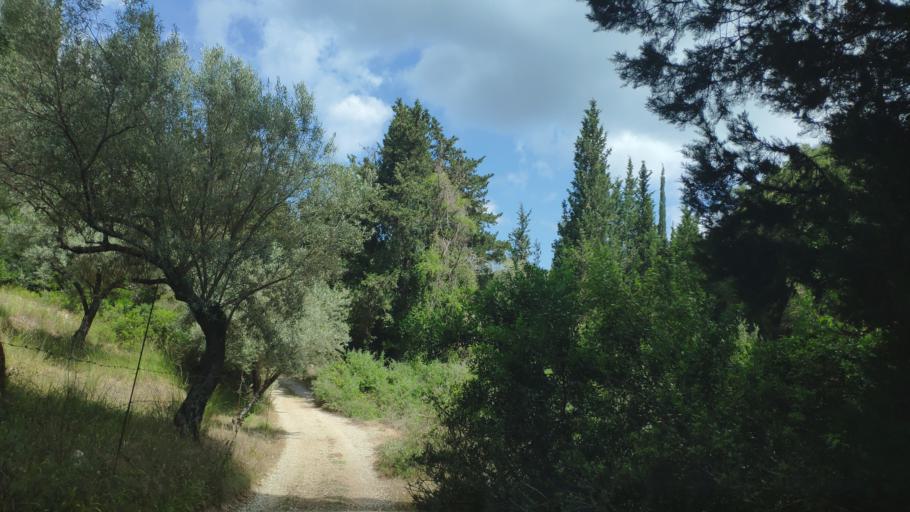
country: GR
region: Ionian Islands
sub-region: Lefkada
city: Lefkada
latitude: 38.7995
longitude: 20.6723
